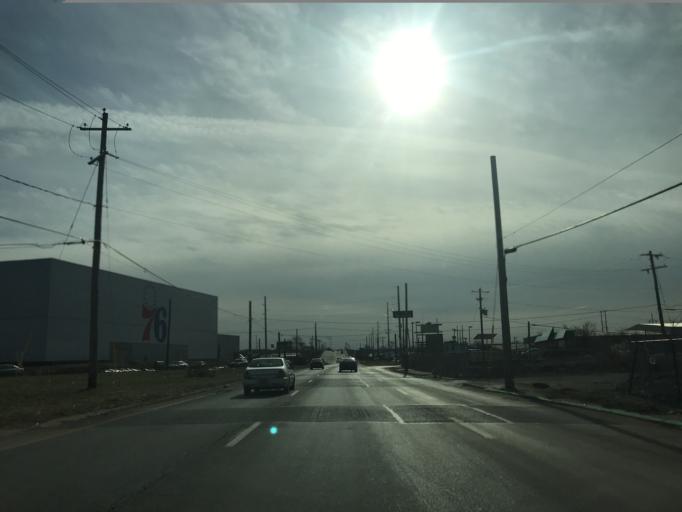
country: US
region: Delaware
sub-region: New Castle County
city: Wilmington
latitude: 39.7289
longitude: -75.5561
